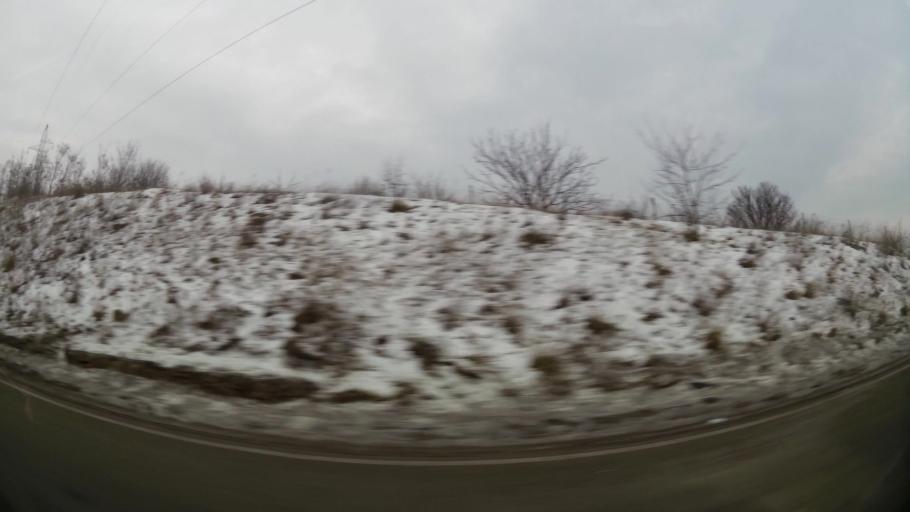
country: MK
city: Kondovo
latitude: 42.0346
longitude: 21.3332
